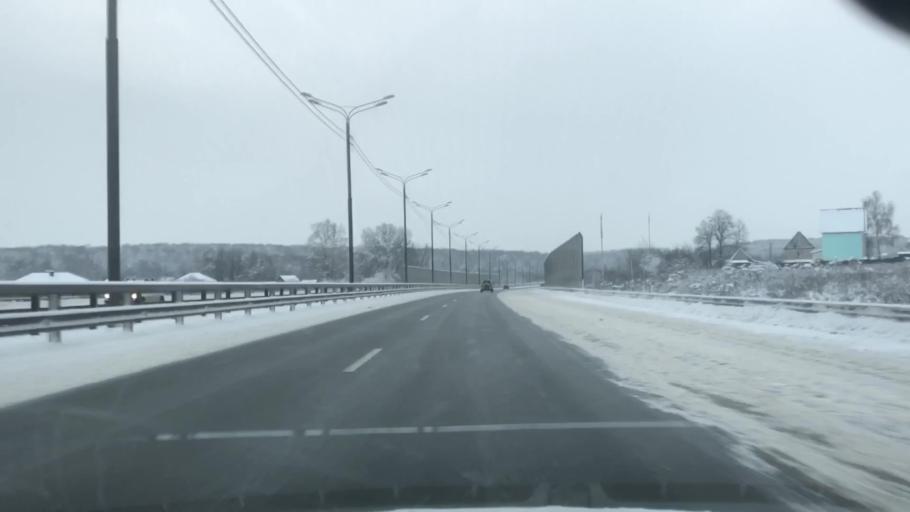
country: RU
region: Moskovskaya
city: Barybino
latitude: 55.2814
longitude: 37.8620
